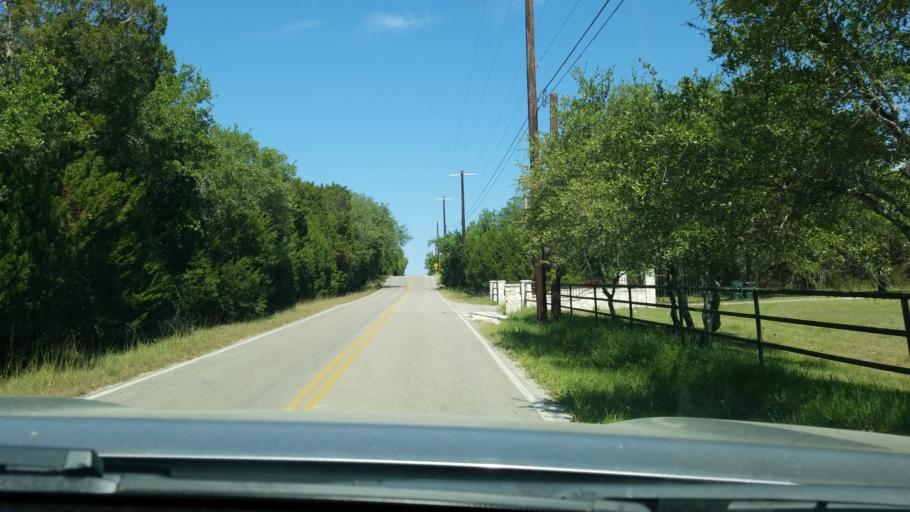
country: US
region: Texas
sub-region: Comal County
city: Bulverde
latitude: 29.7590
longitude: -98.4907
